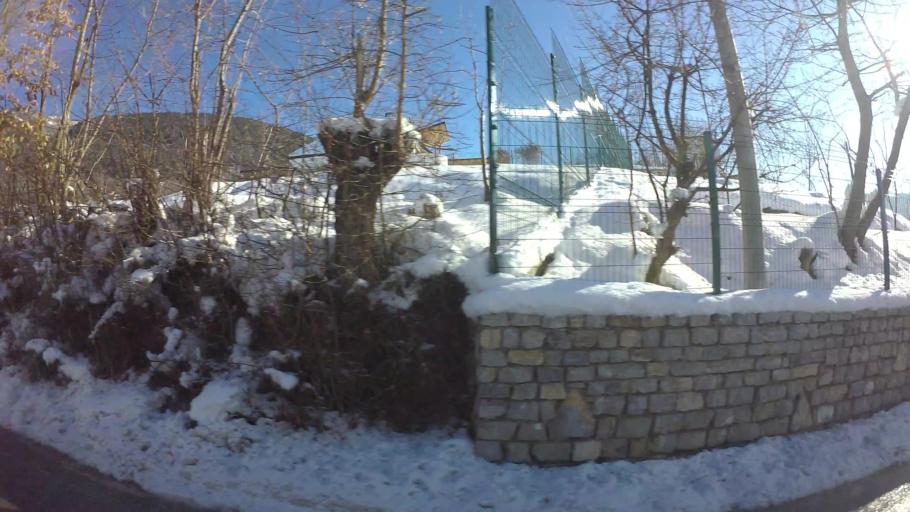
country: BA
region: Federation of Bosnia and Herzegovina
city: Kobilja Glava
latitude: 43.8944
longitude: 18.4158
